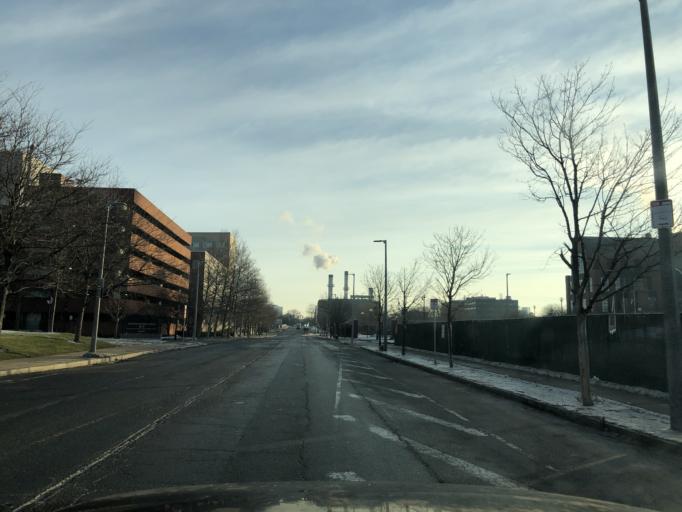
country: US
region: Massachusetts
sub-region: Middlesex County
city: Cambridge
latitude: 42.3639
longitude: -71.1210
